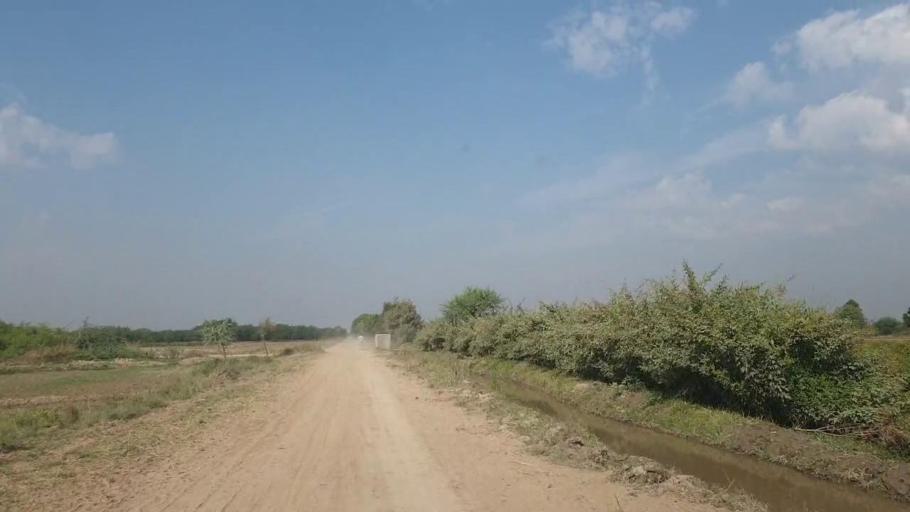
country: PK
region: Sindh
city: Digri
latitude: 25.0237
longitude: 69.0710
